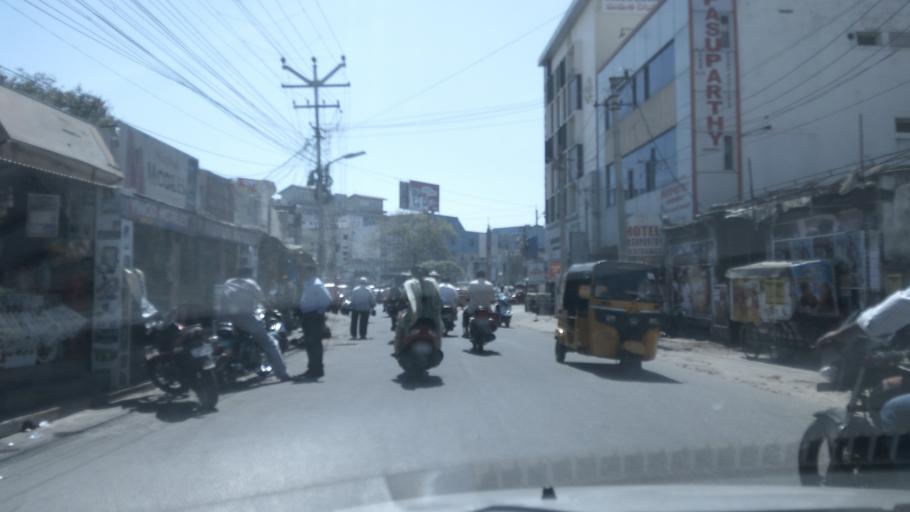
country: IN
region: Andhra Pradesh
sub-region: Chittoor
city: Tirupati
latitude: 13.6297
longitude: 79.4239
